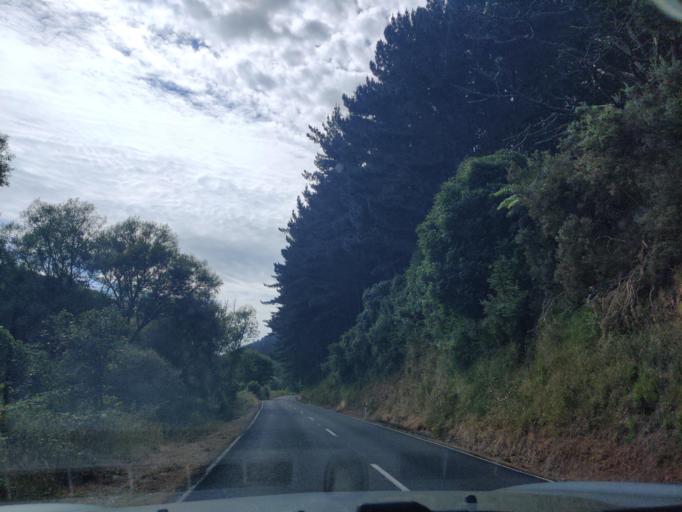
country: NZ
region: Waikato
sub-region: Otorohanga District
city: Otorohanga
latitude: -38.0958
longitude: 175.1139
